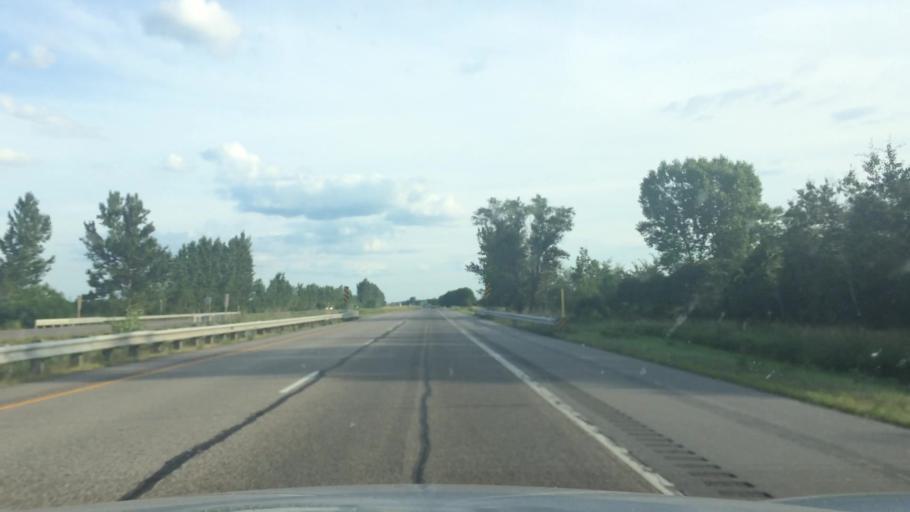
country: US
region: Wisconsin
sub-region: Portage County
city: Plover
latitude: 44.3389
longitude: -89.5228
